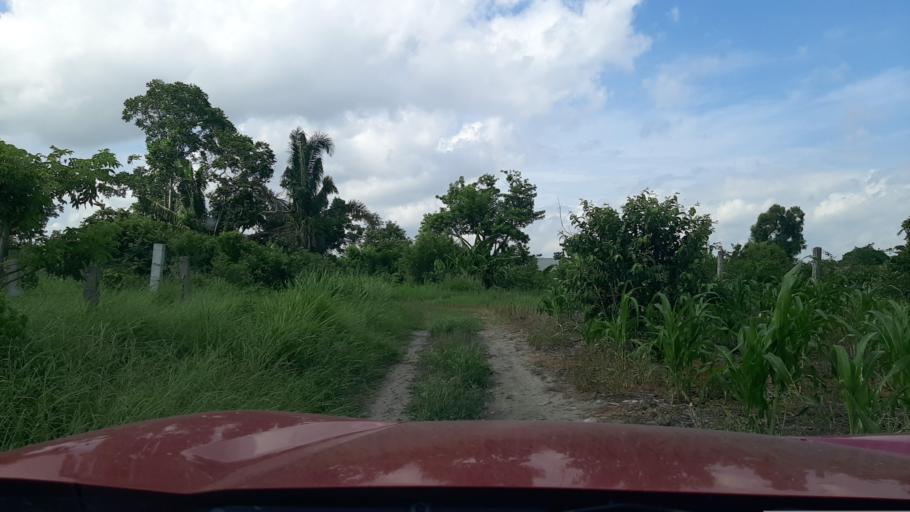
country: MX
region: Veracruz
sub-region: Poza Rica de Hidalgo
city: Villa de las Flores
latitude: 20.5734
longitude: -97.4359
